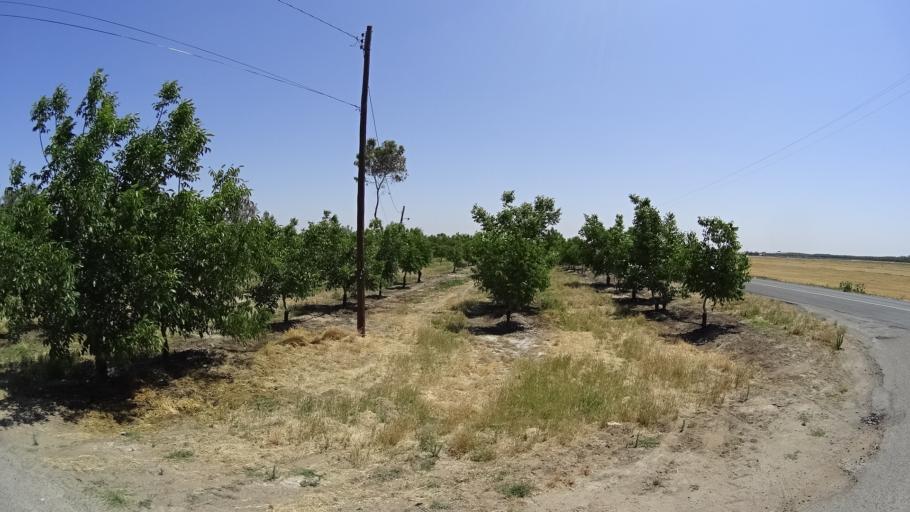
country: US
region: California
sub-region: Kings County
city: Armona
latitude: 36.2839
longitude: -119.6904
